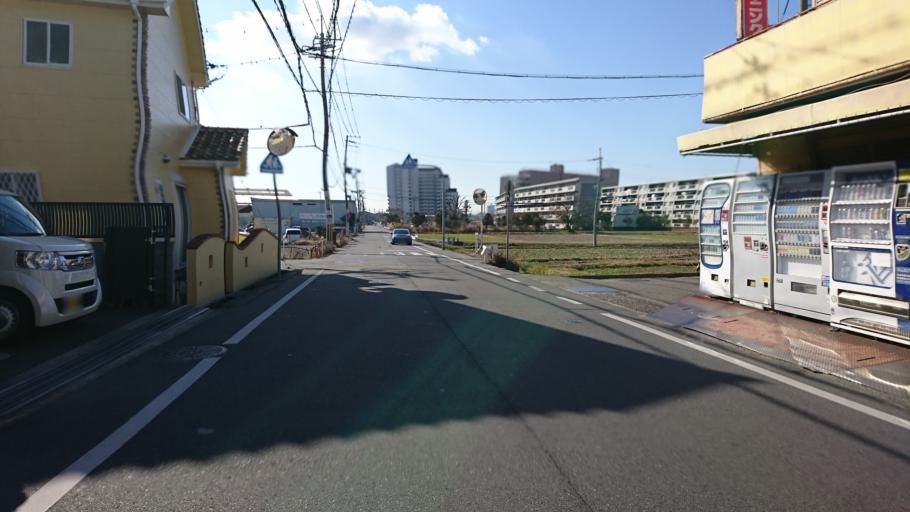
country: JP
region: Hyogo
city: Kakogawacho-honmachi
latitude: 34.7338
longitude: 134.8691
